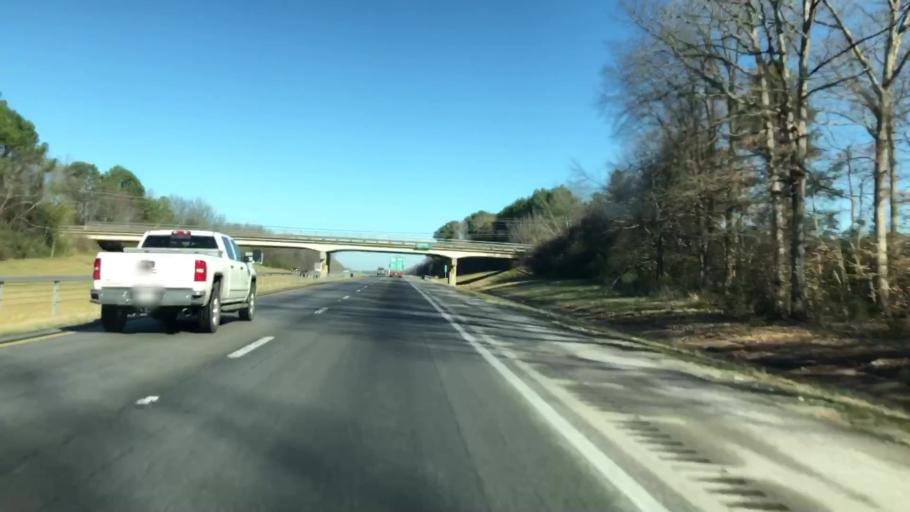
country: US
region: Alabama
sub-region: Limestone County
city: Athens
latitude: 34.7958
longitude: -86.9390
